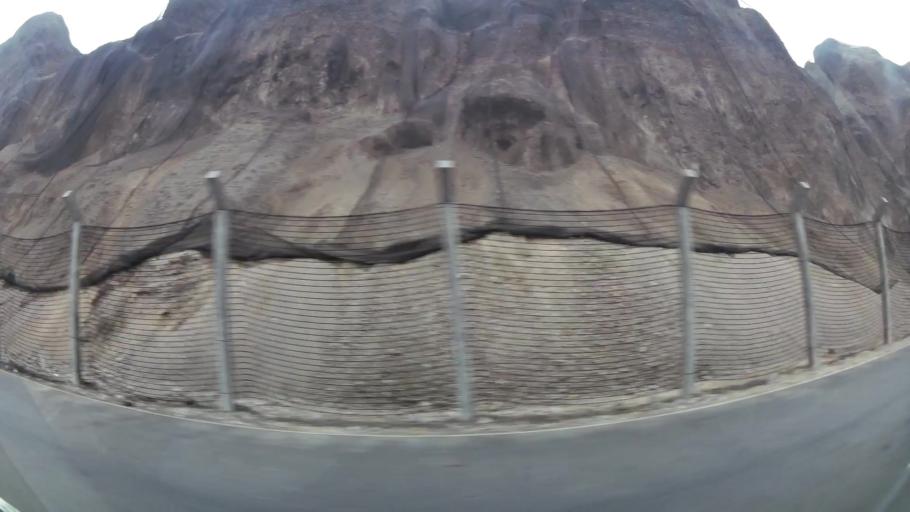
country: PE
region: Lima
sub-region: Lima
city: San Isidro
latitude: -12.1232
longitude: -77.0423
